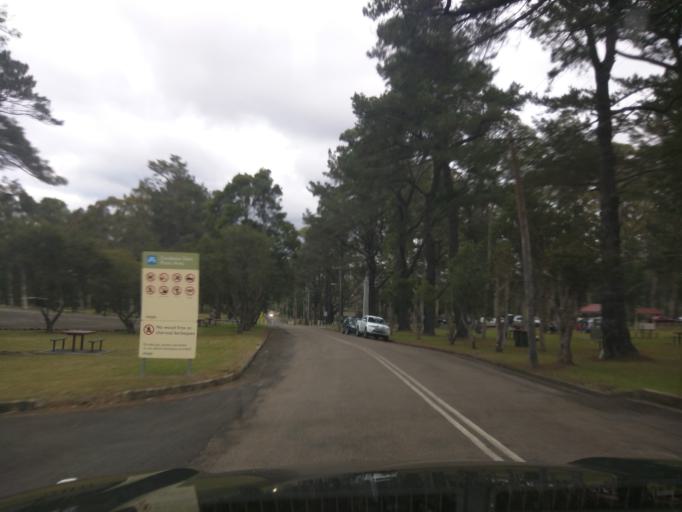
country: AU
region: New South Wales
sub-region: Wollongong
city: Mount Keira
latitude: -34.3252
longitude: 150.7462
